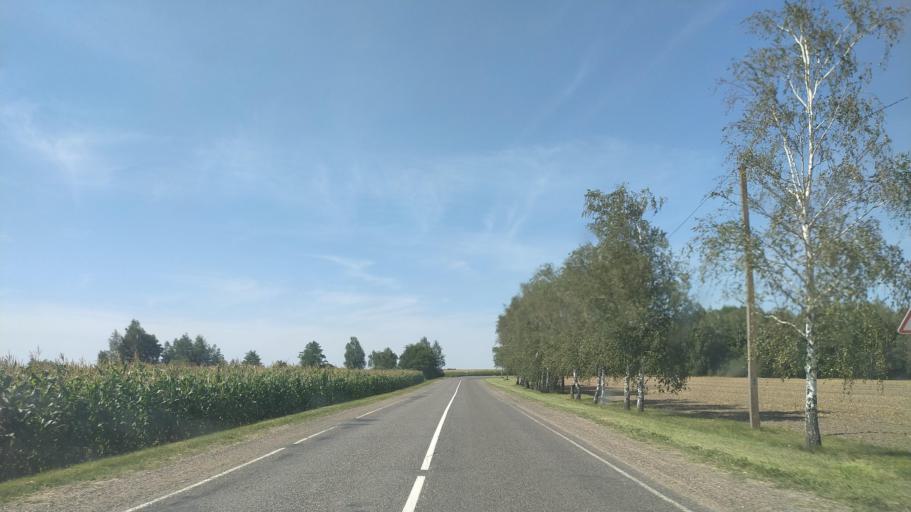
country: BY
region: Brest
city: Byaroza
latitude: 52.3942
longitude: 25.0100
